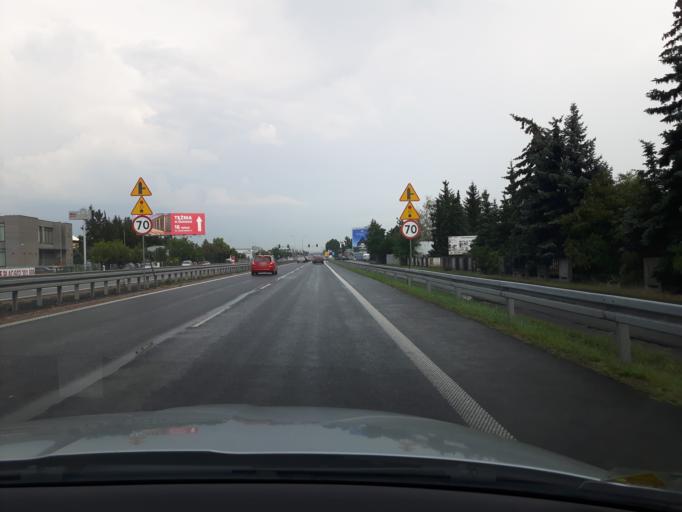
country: PL
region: Masovian Voivodeship
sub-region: Powiat warszawski zachodni
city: Lomianki
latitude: 52.3367
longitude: 20.8782
